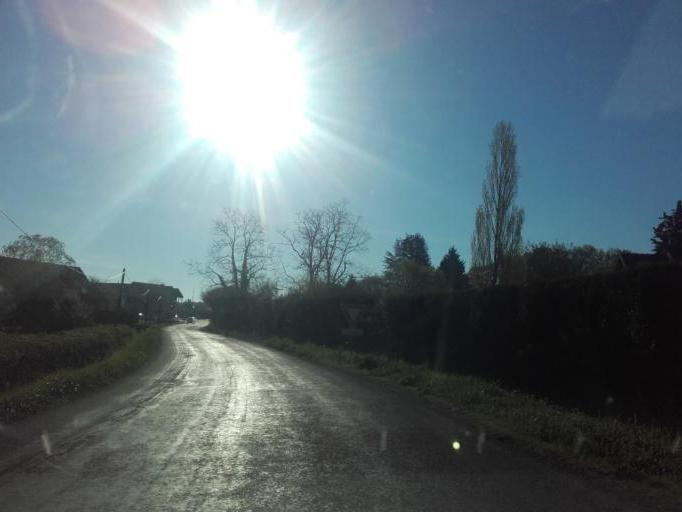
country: FR
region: Bourgogne
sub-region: Departement de Saone-et-Loire
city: Dracy-le-Fort
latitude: 46.8149
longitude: 4.7497
